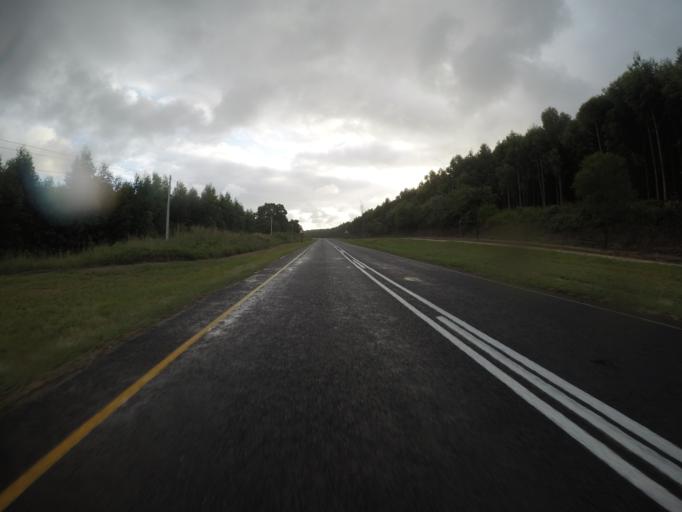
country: ZA
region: KwaZulu-Natal
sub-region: uMkhanyakude District Municipality
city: Mtubatuba
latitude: -28.3688
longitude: 32.2586
